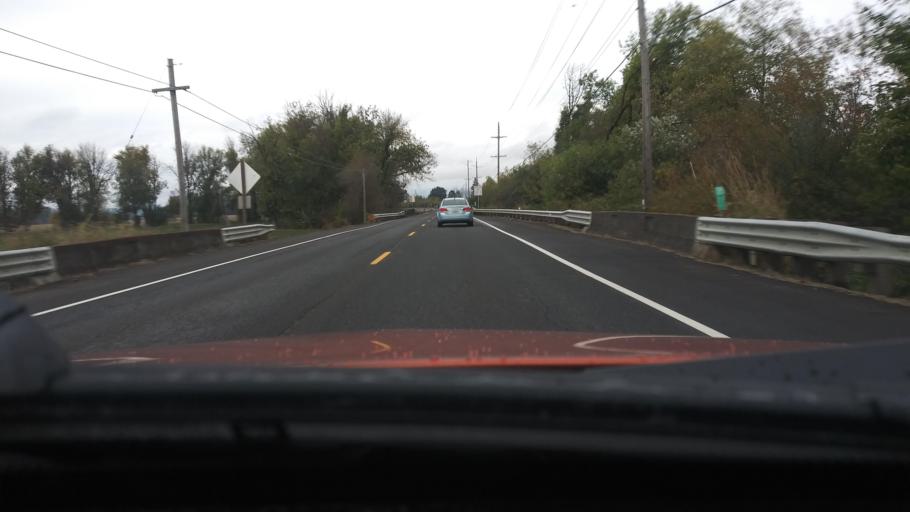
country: US
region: Oregon
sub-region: Washington County
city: Banks
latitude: 45.5709
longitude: -123.1094
